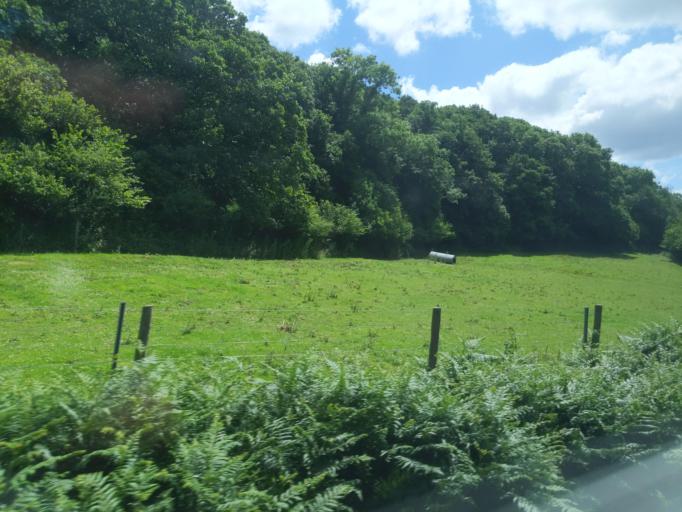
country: GB
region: England
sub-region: Cornwall
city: Lostwithiel
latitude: 50.3884
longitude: -4.6676
